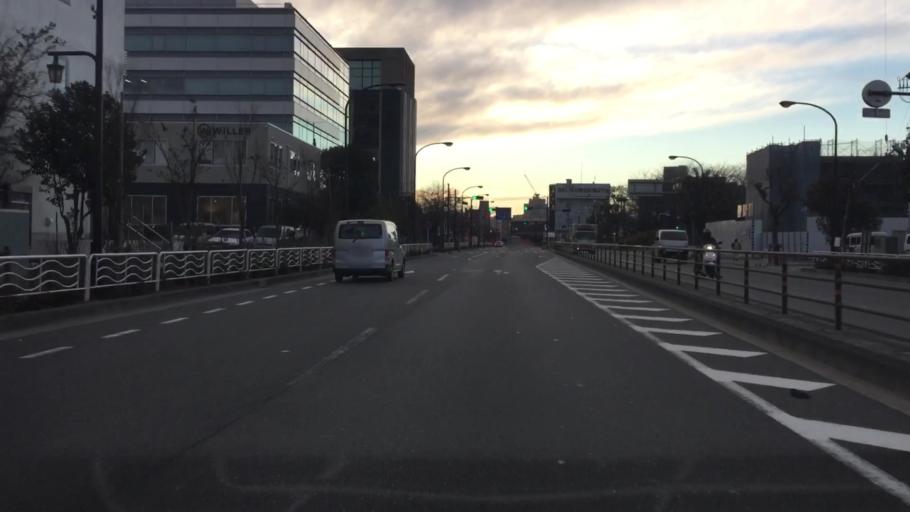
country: JP
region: Tokyo
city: Urayasu
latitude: 35.6448
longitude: 139.8284
